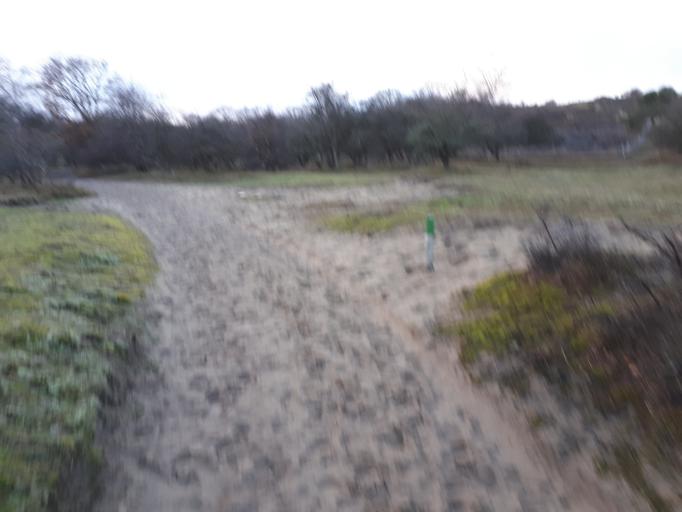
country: NL
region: South Holland
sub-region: Gemeente Wassenaar
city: Wassenaar
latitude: 52.1417
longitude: 4.3559
